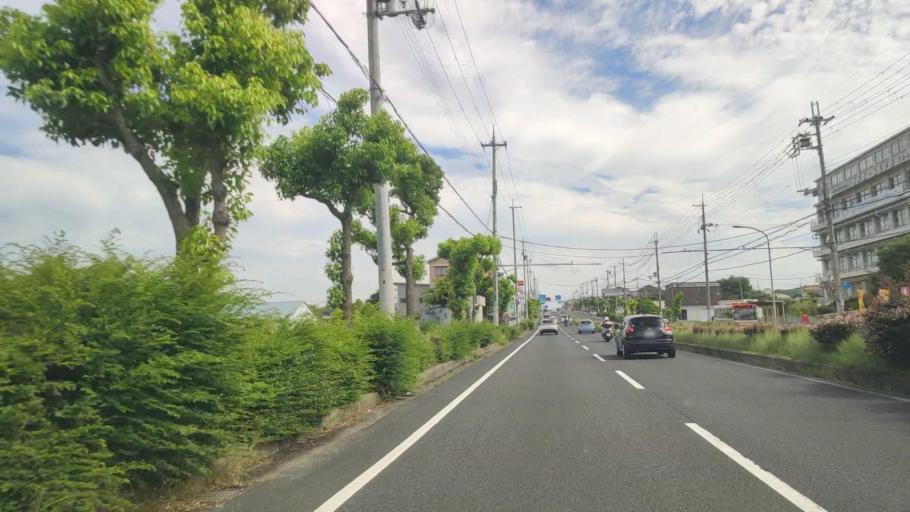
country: JP
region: Hyogo
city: Akashi
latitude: 34.6924
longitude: 134.9829
